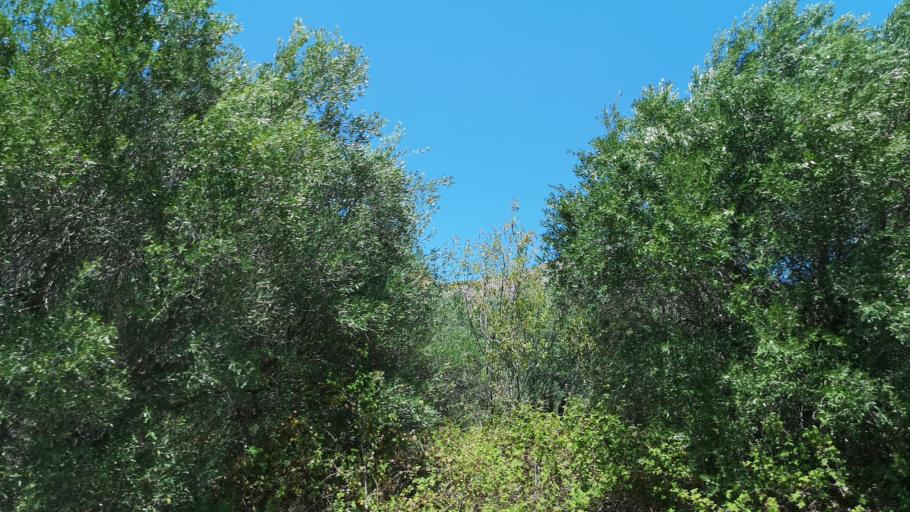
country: GR
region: Crete
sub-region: Nomos Lasithiou
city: Neapoli
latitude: 35.2473
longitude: 25.6293
